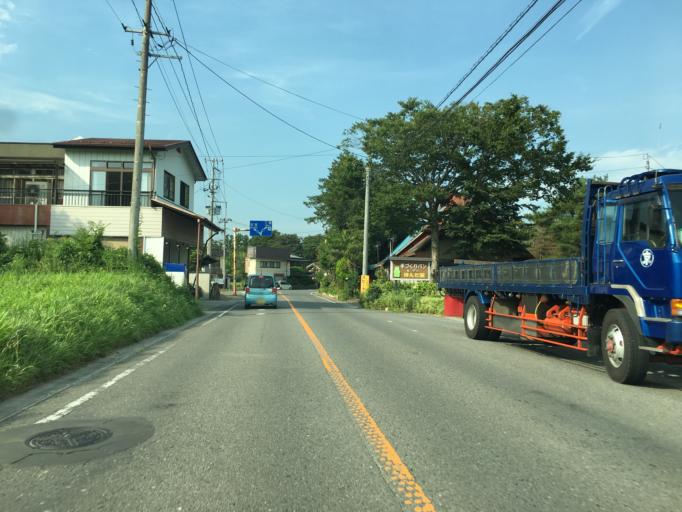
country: JP
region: Fukushima
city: Miharu
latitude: 37.4514
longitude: 140.4291
